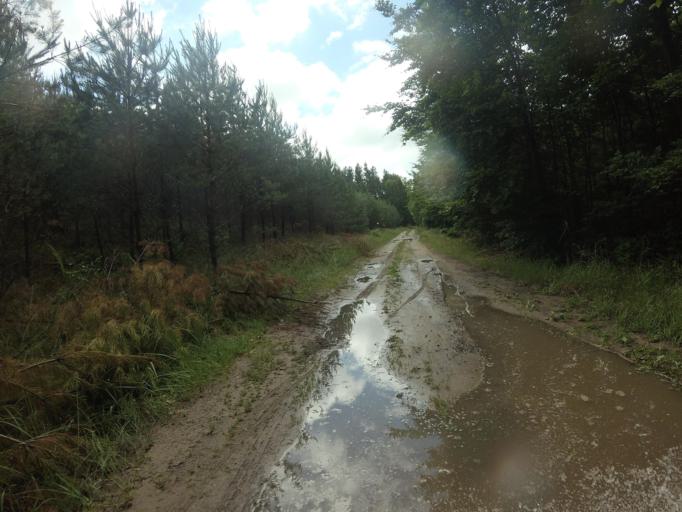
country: PL
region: West Pomeranian Voivodeship
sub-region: Powiat choszczenski
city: Bierzwnik
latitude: 53.0117
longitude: 15.5916
